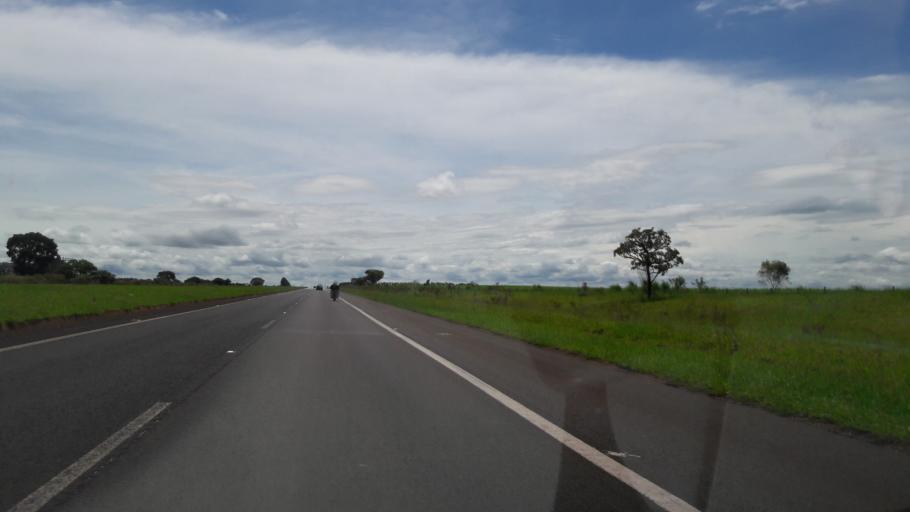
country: BR
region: Sao Paulo
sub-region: Avare
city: Avare
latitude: -22.9403
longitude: -48.9195
